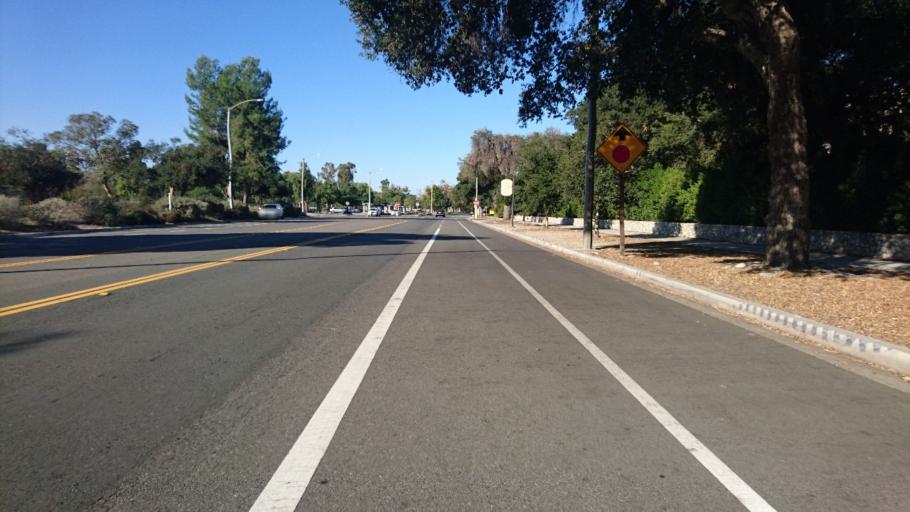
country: US
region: California
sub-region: Los Angeles County
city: Claremont
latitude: 34.0948
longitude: -117.7099
